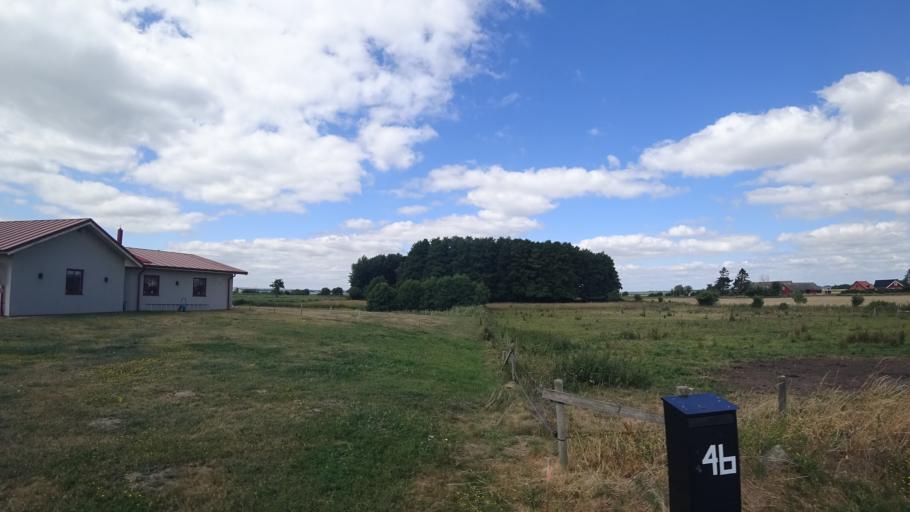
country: SE
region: Skane
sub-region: Kristianstads Kommun
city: Ahus
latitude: 55.9745
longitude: 14.2640
